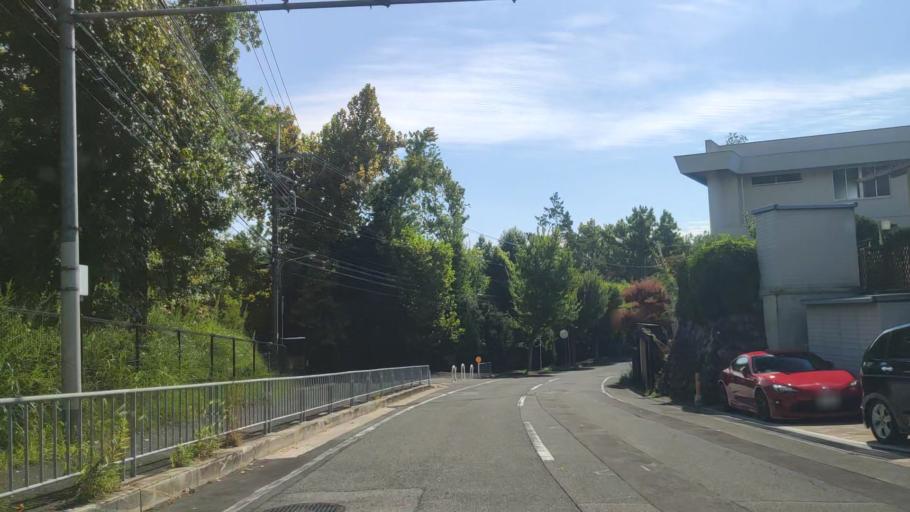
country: JP
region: Osaka
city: Mino
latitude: 34.8245
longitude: 135.5143
